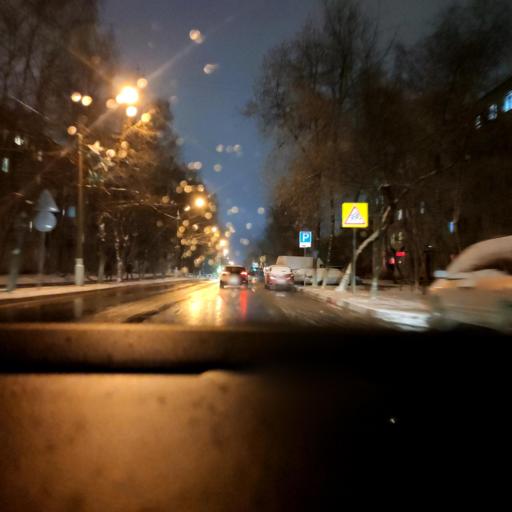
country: RU
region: Moskovskaya
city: Reutov
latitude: 55.7658
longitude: 37.8639
